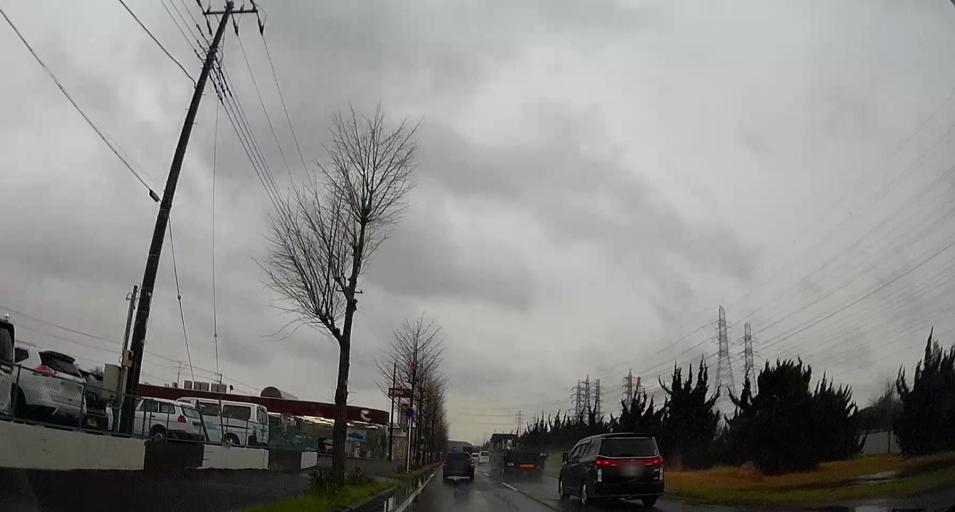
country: JP
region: Chiba
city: Ichihara
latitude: 35.4776
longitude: 140.0331
